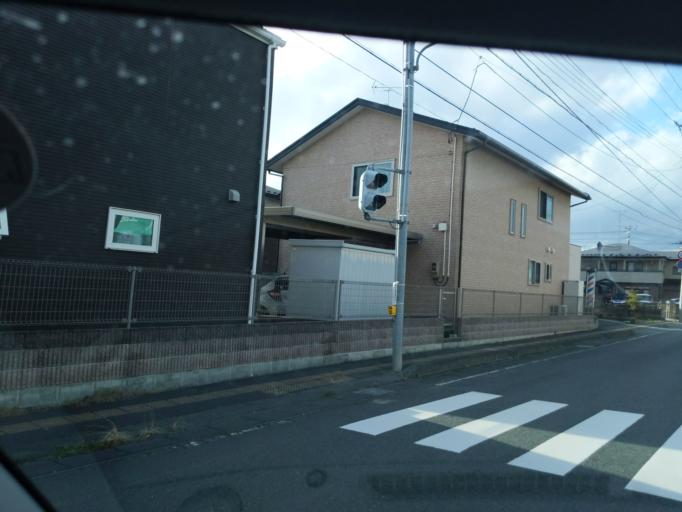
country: JP
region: Iwate
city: Mizusawa
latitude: 39.1388
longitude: 141.1564
